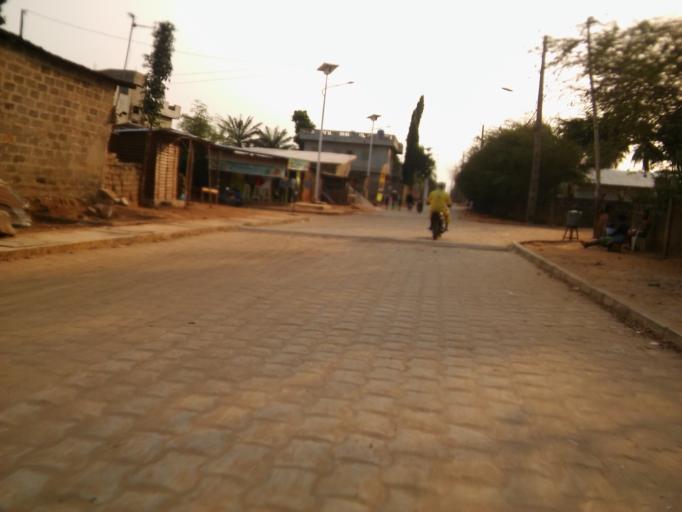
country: BJ
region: Atlantique
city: Abomey-Calavi
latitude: 6.4069
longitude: 2.3320
